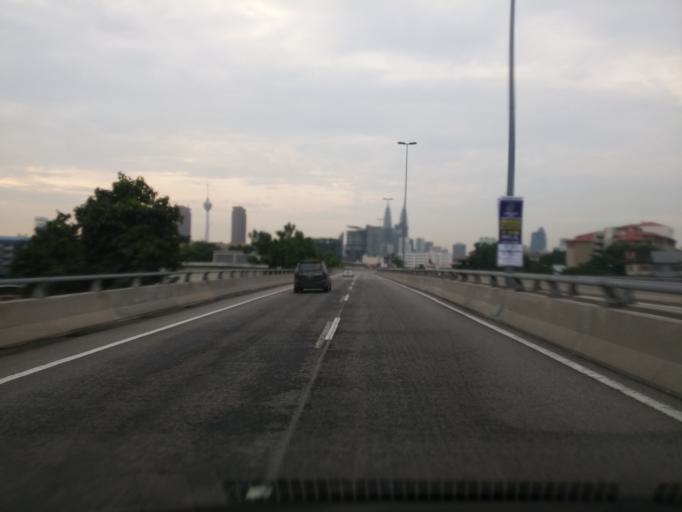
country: MY
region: Kuala Lumpur
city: Kuala Lumpur
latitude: 3.1287
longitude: 101.7187
